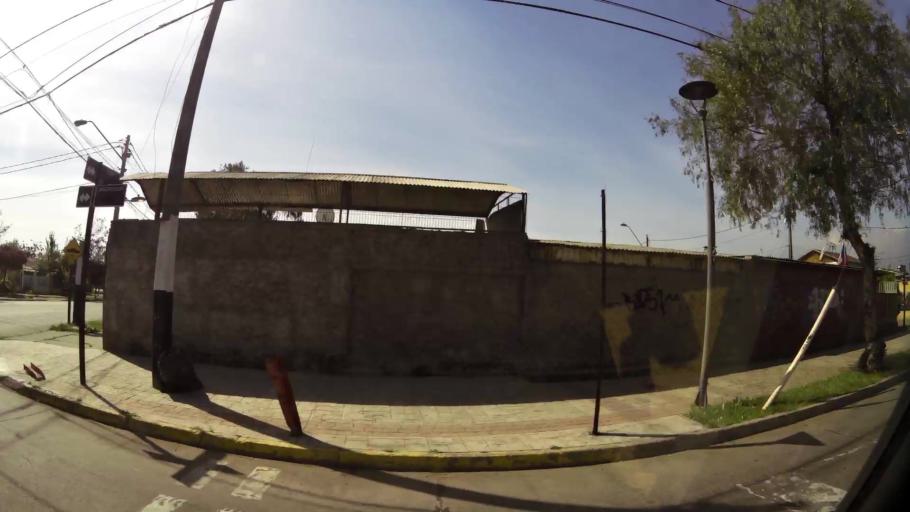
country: CL
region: Santiago Metropolitan
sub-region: Provincia de Santiago
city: La Pintana
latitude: -33.5415
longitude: -70.6284
